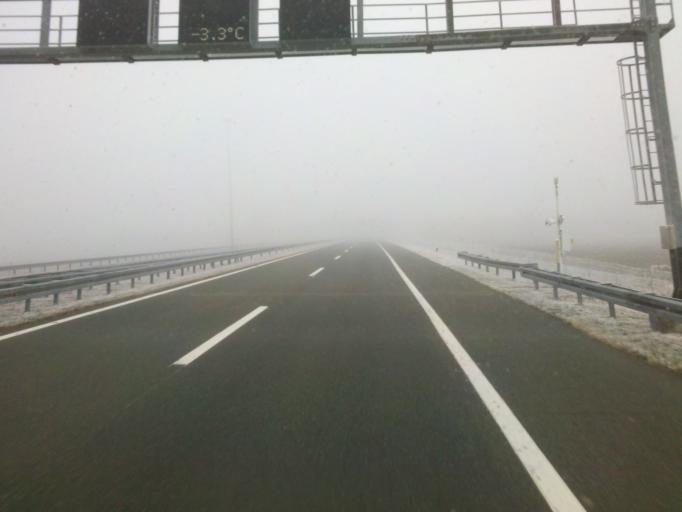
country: HR
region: Medimurska
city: Orehovica
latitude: 46.3458
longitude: 16.5322
